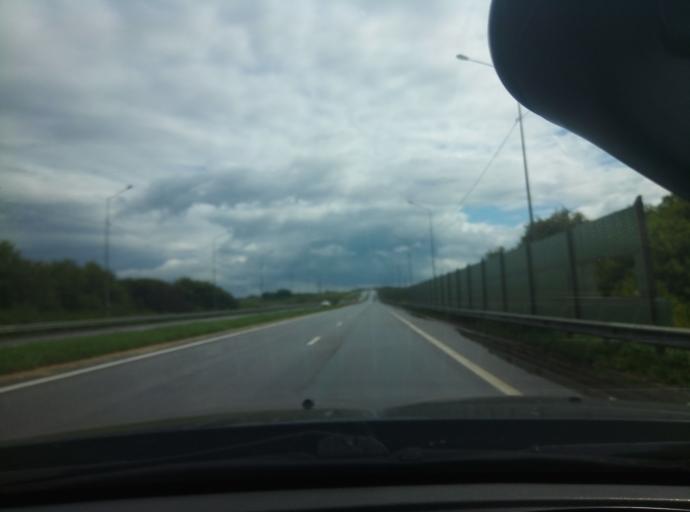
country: RU
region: Tula
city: Kamenetskiy
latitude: 54.0395
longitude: 38.2057
